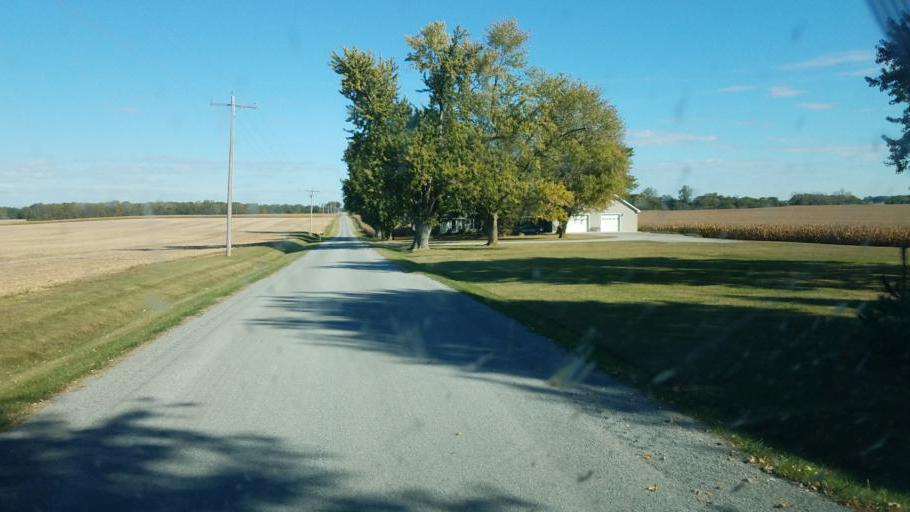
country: US
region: Ohio
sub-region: Wyandot County
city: Upper Sandusky
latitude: 40.7181
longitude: -83.2072
